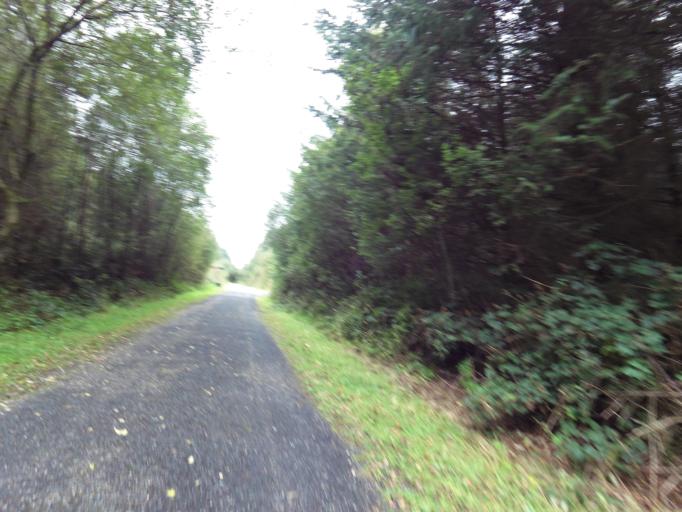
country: IE
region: Leinster
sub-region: Uibh Fhaili
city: Ferbane
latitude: 53.2136
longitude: -7.7501
